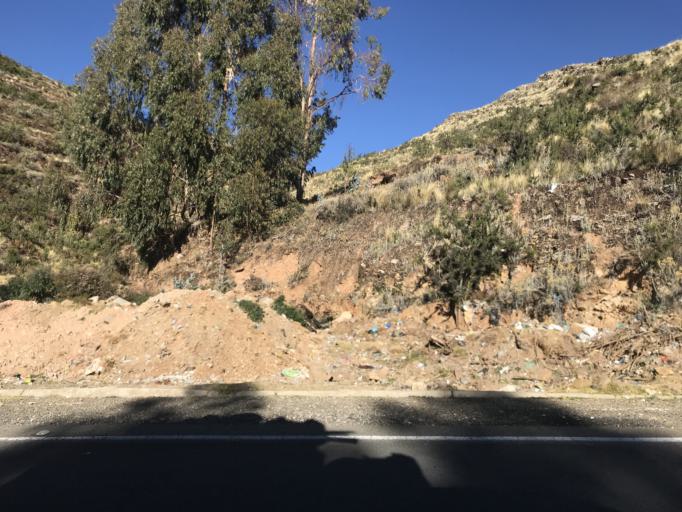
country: BO
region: La Paz
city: San Pedro
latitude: -16.2267
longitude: -68.8541
